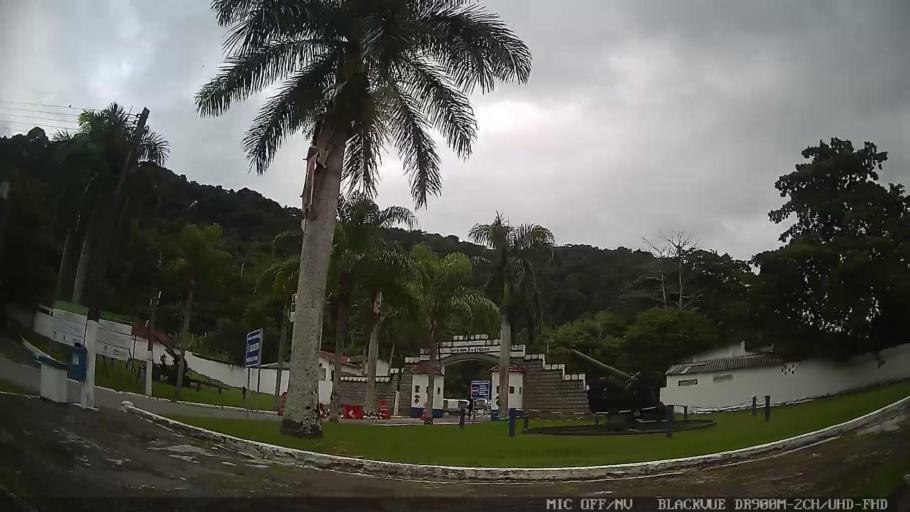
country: BR
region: Sao Paulo
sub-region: Guaruja
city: Guaruja
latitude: -24.0151
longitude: -46.2784
